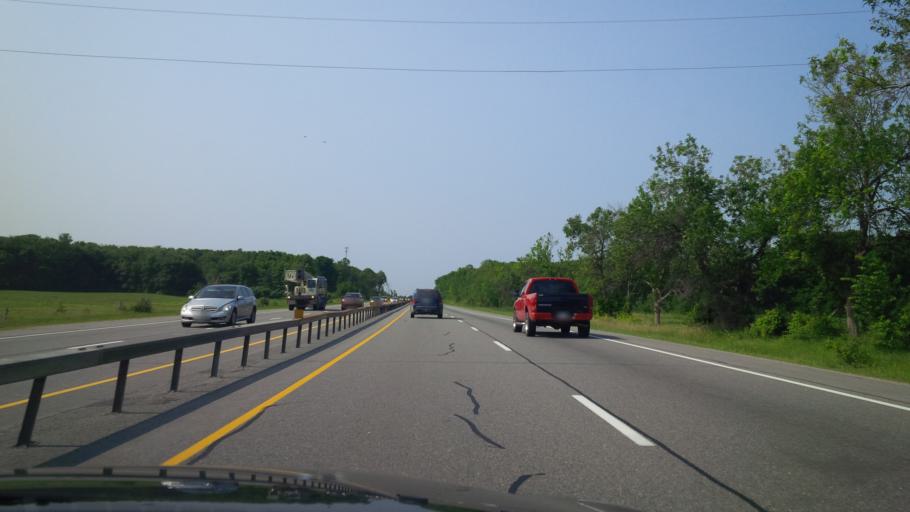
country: CA
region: Ontario
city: Orillia
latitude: 44.5308
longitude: -79.4613
